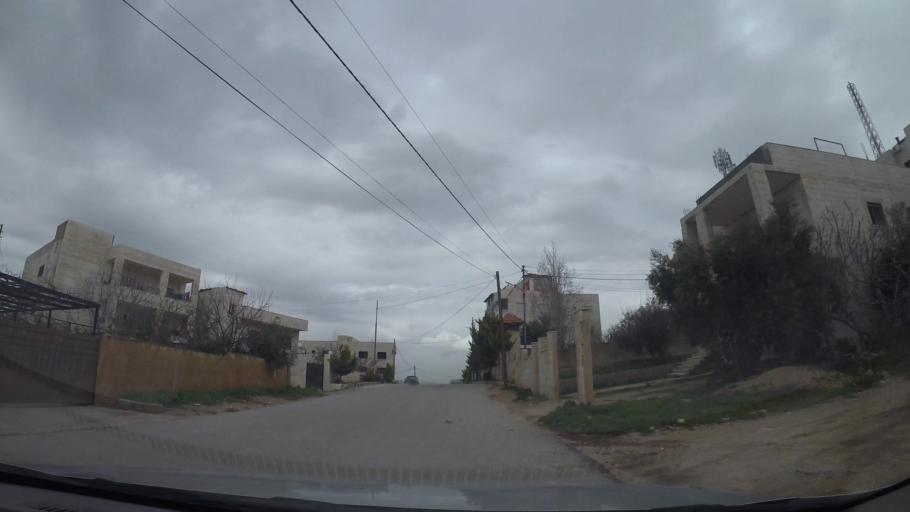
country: JO
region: Amman
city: Umm as Summaq
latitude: 31.9108
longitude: 35.8447
